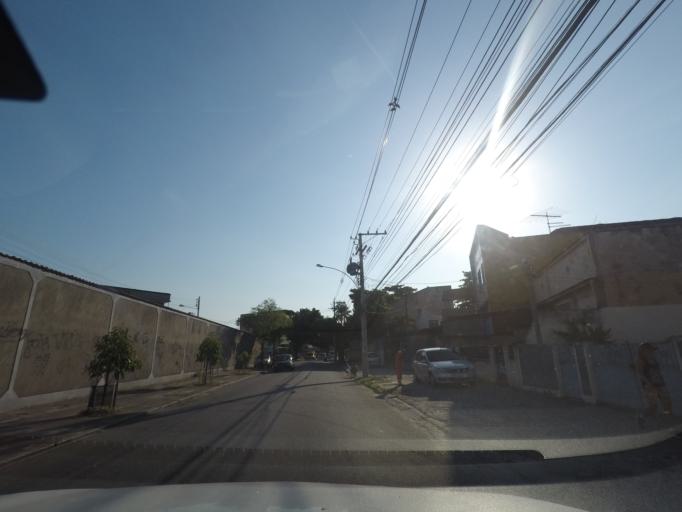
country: BR
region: Rio de Janeiro
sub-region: Rio De Janeiro
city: Rio de Janeiro
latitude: -22.8455
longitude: -43.2557
